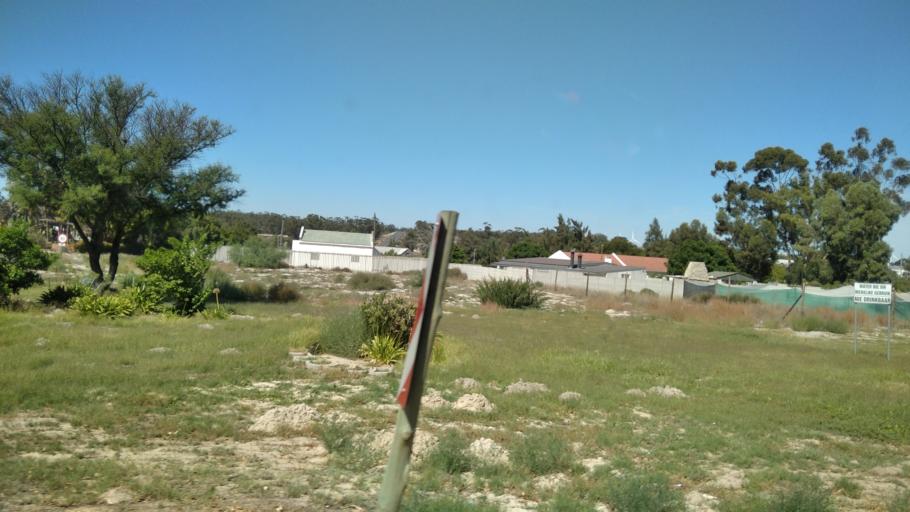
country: ZA
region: Western Cape
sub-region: West Coast District Municipality
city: Moorreesburg
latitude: -33.0562
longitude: 18.3432
